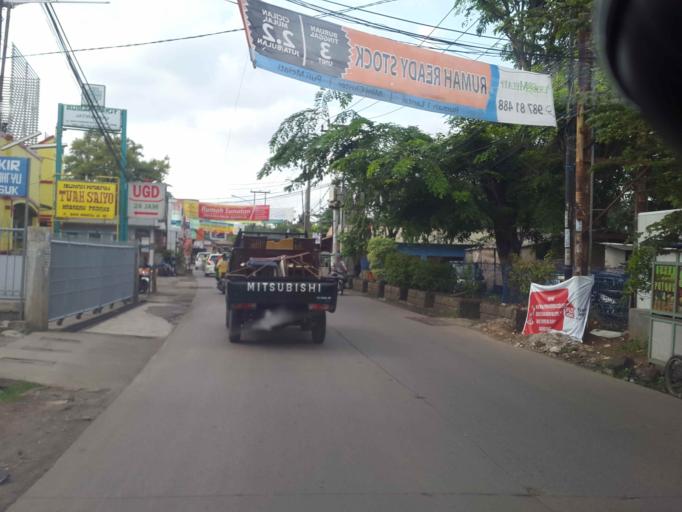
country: ID
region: West Java
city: Bekasi
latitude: -6.2964
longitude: 106.9215
